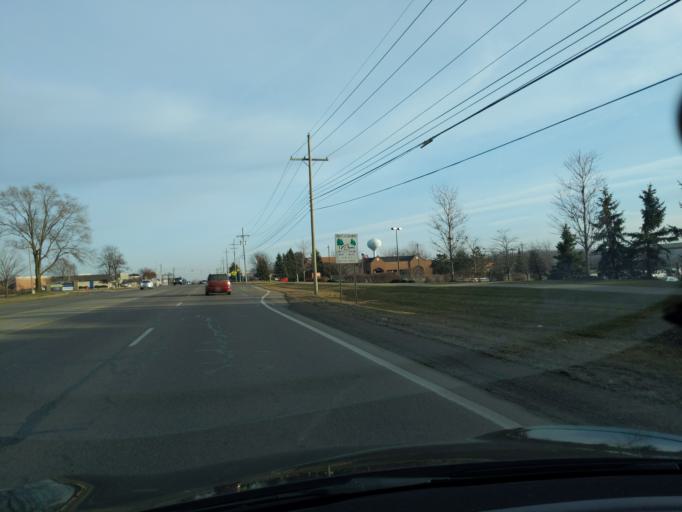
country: US
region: Michigan
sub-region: Livingston County
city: Howell
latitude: 42.5918
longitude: -83.8880
